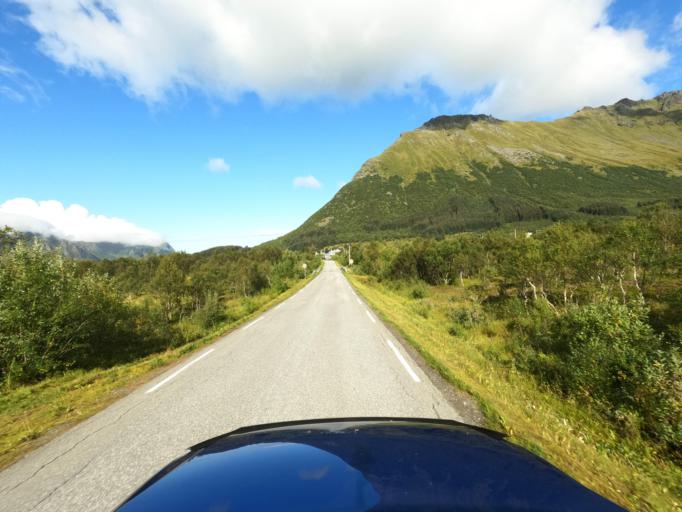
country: NO
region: Nordland
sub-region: Vagan
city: Kabelvag
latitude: 68.2829
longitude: 14.3498
